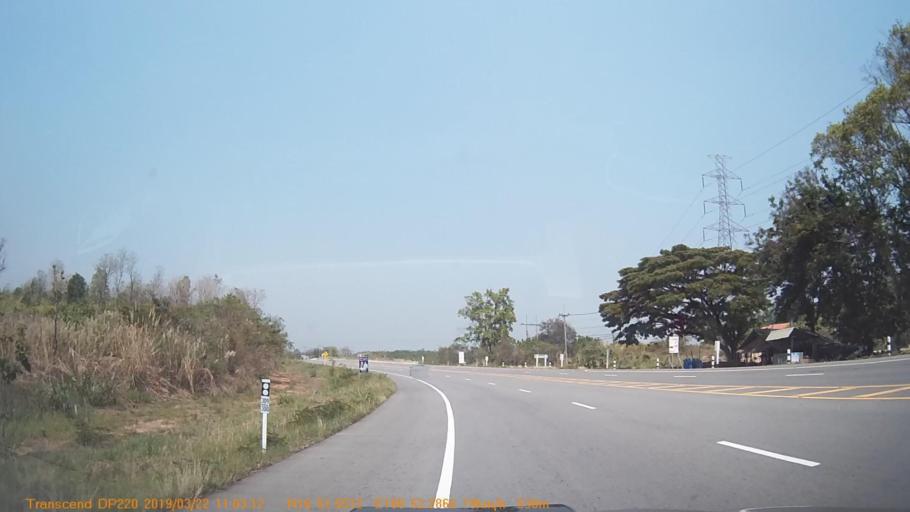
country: TH
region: Phitsanulok
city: Nakhon Thai
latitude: 16.8592
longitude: 100.8713
